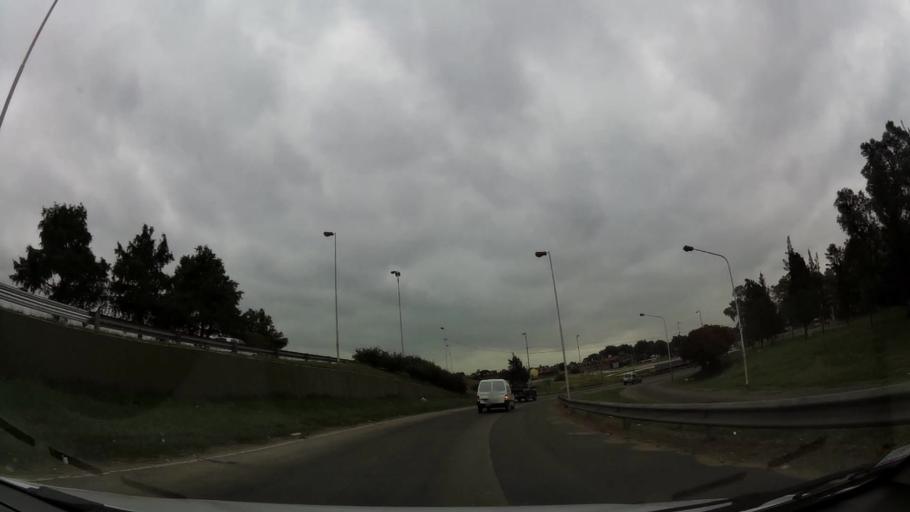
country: AR
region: Buenos Aires F.D.
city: Villa Lugano
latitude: -34.7208
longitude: -58.5132
